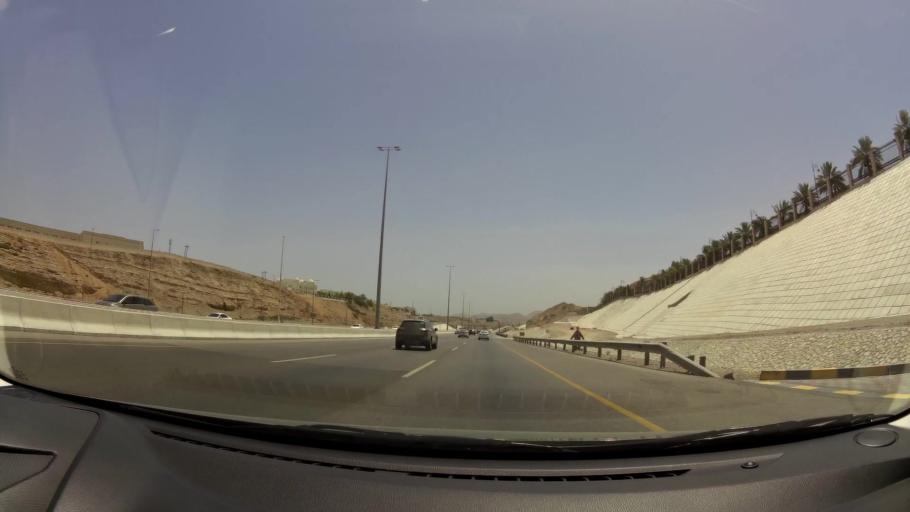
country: OM
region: Muhafazat Masqat
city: Bawshar
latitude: 23.5941
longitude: 58.4724
